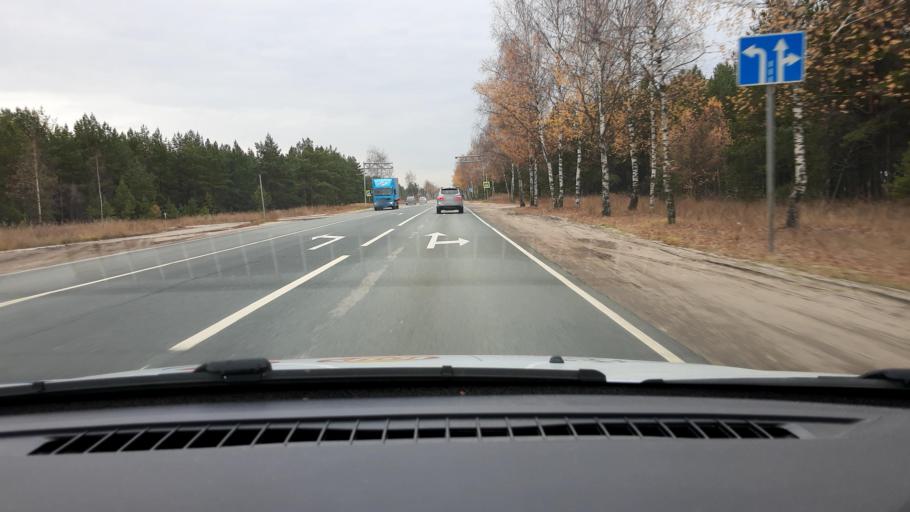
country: RU
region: Nizjnij Novgorod
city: Dzerzhinsk
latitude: 56.2897
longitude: 43.4758
